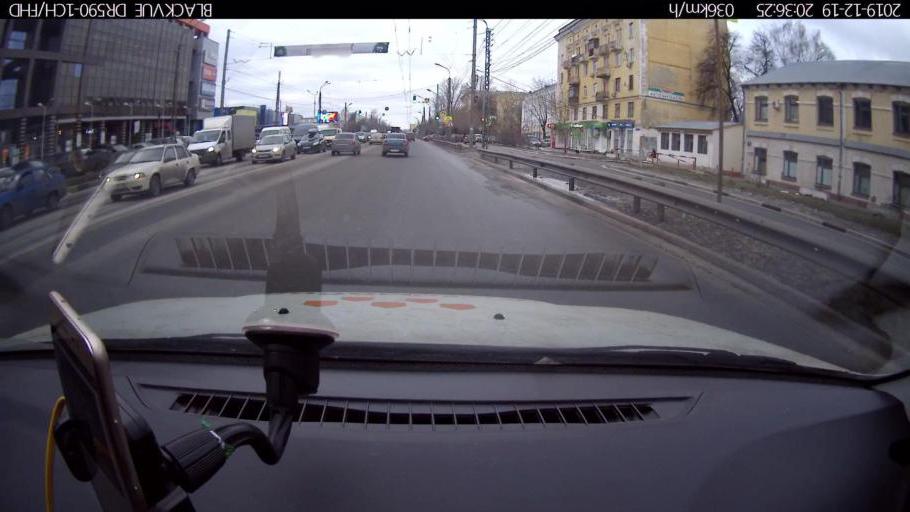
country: RU
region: Nizjnij Novgorod
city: Nizhniy Novgorod
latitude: 56.3190
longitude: 43.9254
